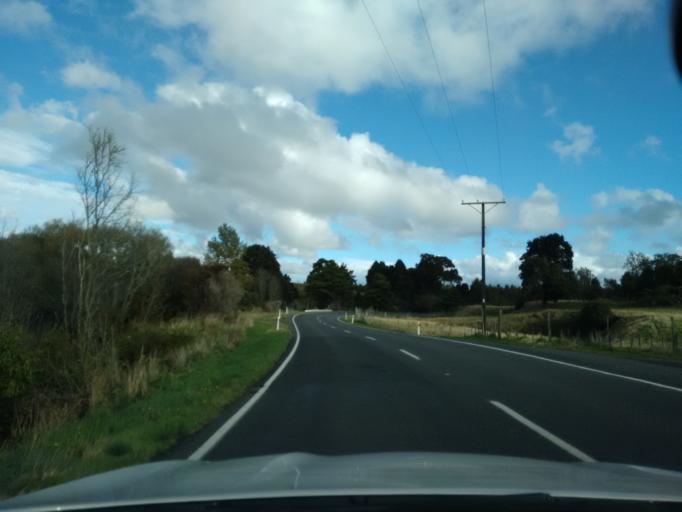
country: NZ
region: Manawatu-Wanganui
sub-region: Ruapehu District
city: Waiouru
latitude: -39.4171
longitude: 175.2840
